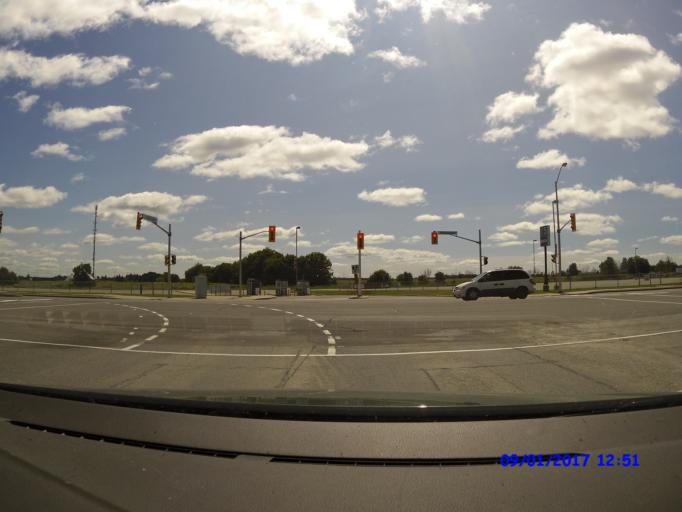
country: CA
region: Ontario
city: Bells Corners
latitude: 45.2969
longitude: -75.9217
